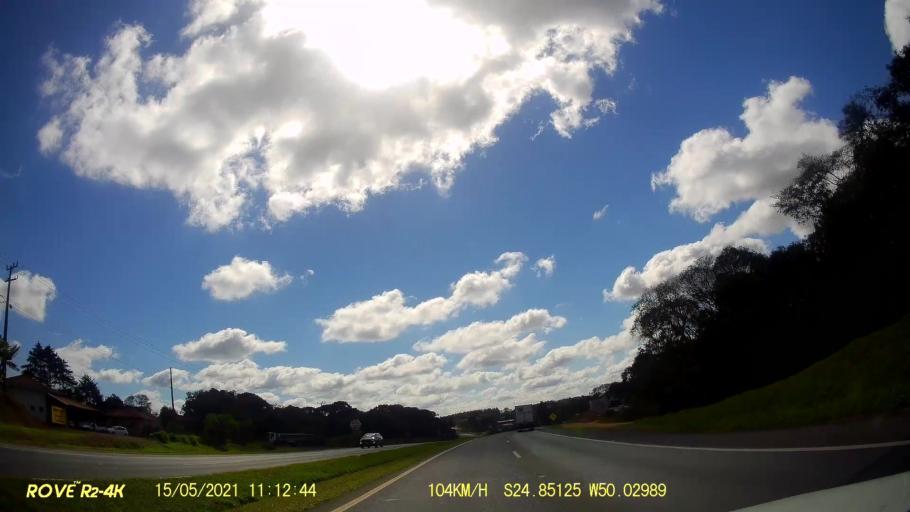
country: BR
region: Parana
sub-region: Castro
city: Castro
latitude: -24.8512
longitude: -50.0298
